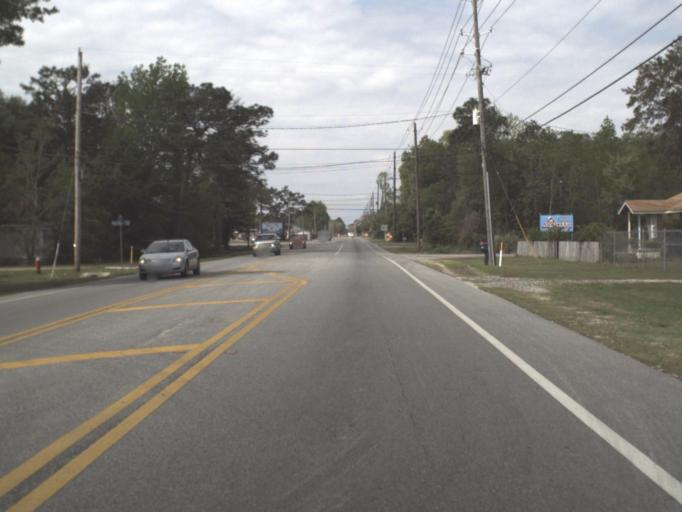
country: US
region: Florida
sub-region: Escambia County
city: Warrington
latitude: 30.3754
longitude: -87.3203
